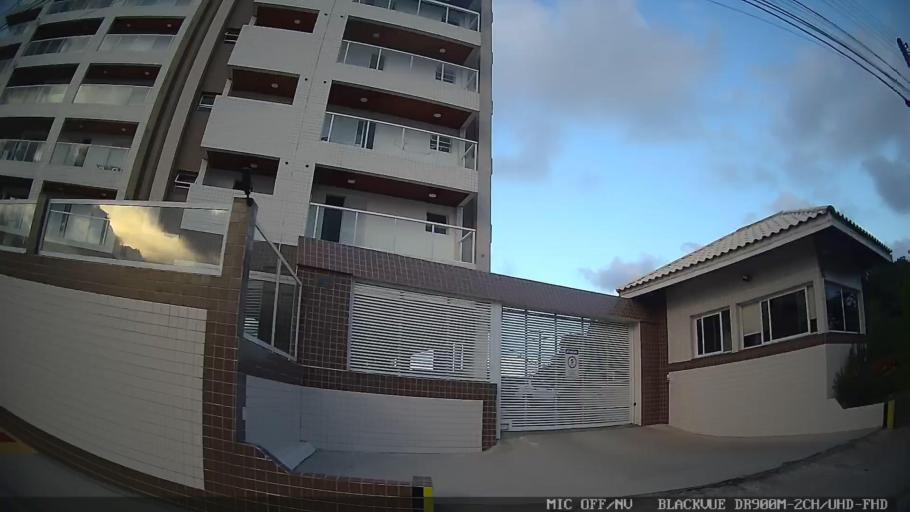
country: BR
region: Sao Paulo
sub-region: Peruibe
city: Peruibe
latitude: -24.3240
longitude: -46.9999
